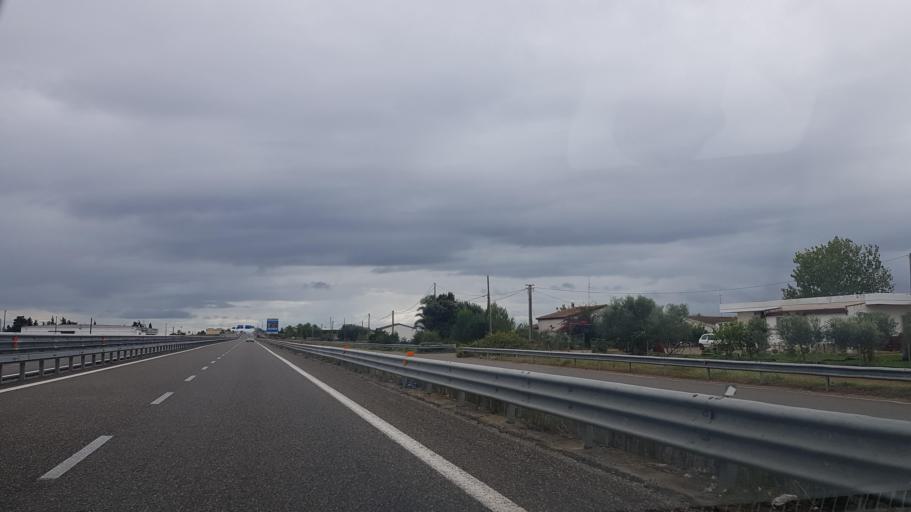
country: IT
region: Apulia
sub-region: Provincia di Taranto
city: Marina di Ginosa
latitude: 40.4087
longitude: 16.8108
